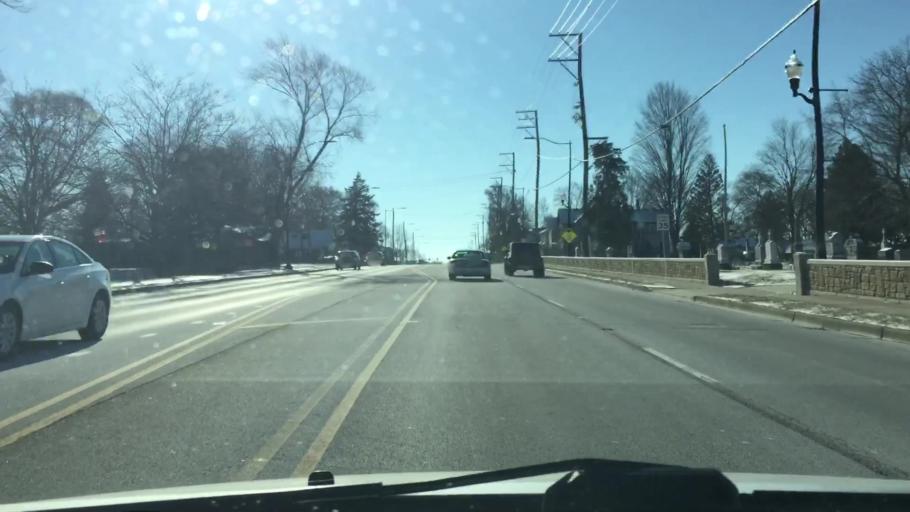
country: US
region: Illinois
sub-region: McHenry County
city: McHenry
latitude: 42.3513
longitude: -88.2674
